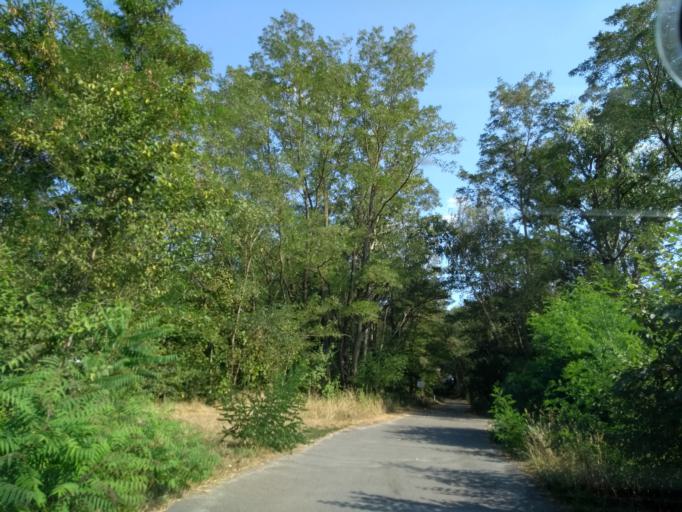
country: DE
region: Brandenburg
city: Luebben
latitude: 51.8521
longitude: 13.8520
